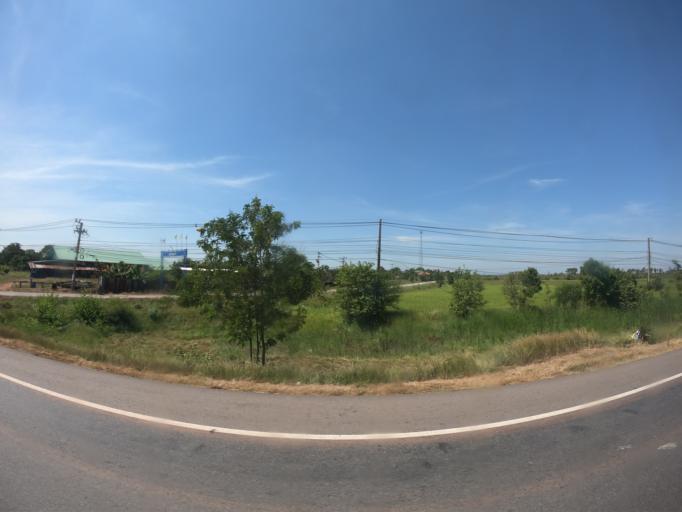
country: TH
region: Khon Kaen
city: Phon
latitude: 15.7860
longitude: 102.6069
